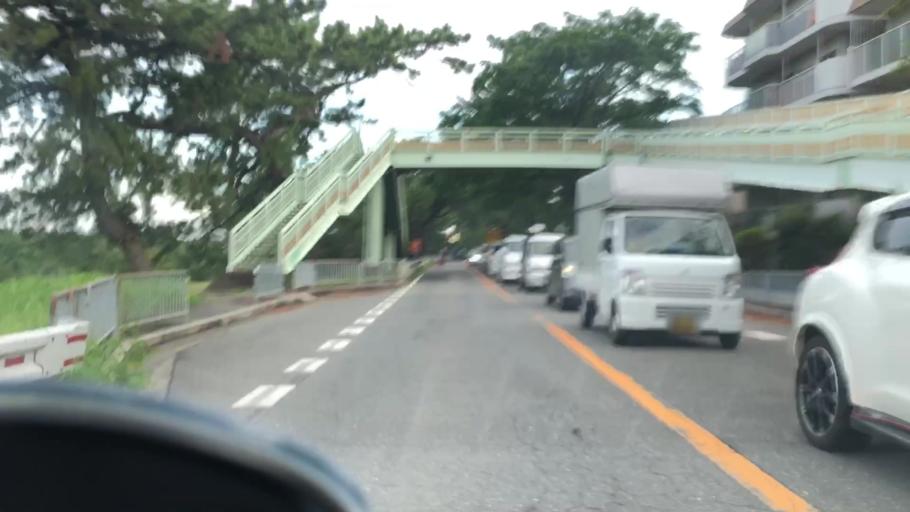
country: JP
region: Hyogo
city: Takarazuka
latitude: 34.7729
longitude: 135.3719
